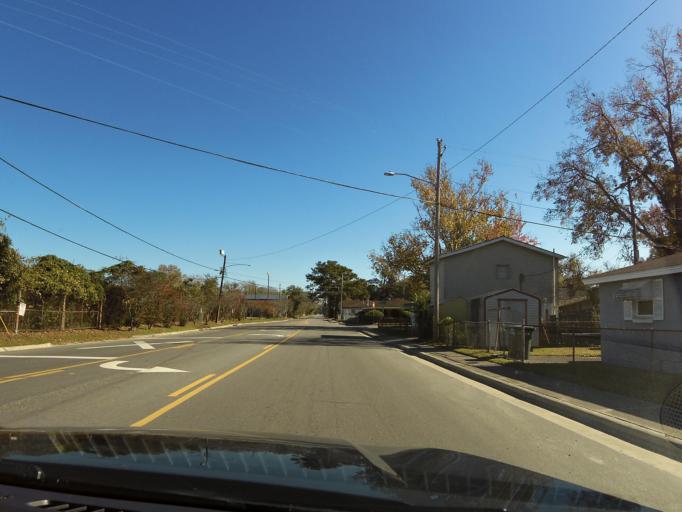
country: US
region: Georgia
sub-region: Chatham County
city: Savannah
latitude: 32.0747
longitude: -81.1244
